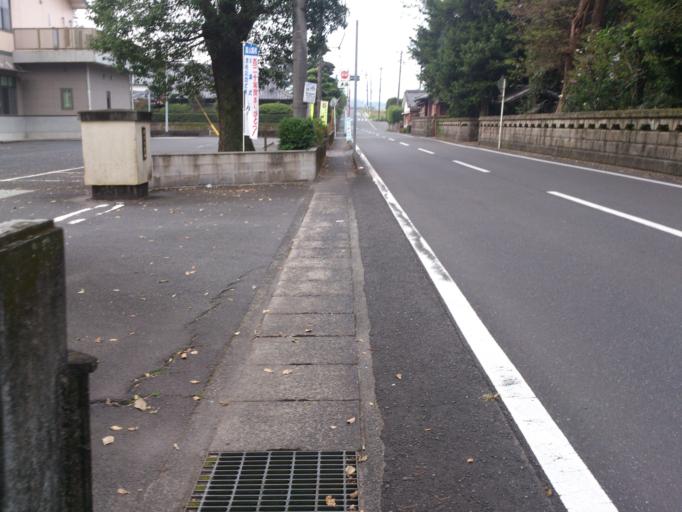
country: JP
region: Kagoshima
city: Kanoya
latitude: 31.3445
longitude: 130.9449
